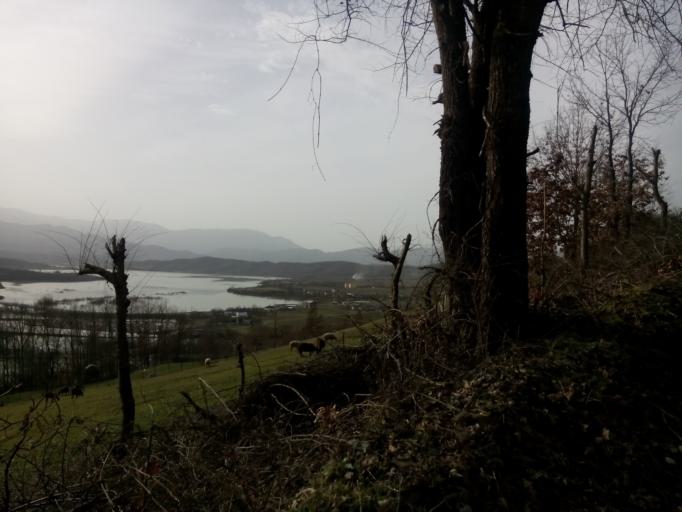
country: AL
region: Diber
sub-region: Rrethi i Matit
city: Rukaj
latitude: 41.6801
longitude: 19.9937
